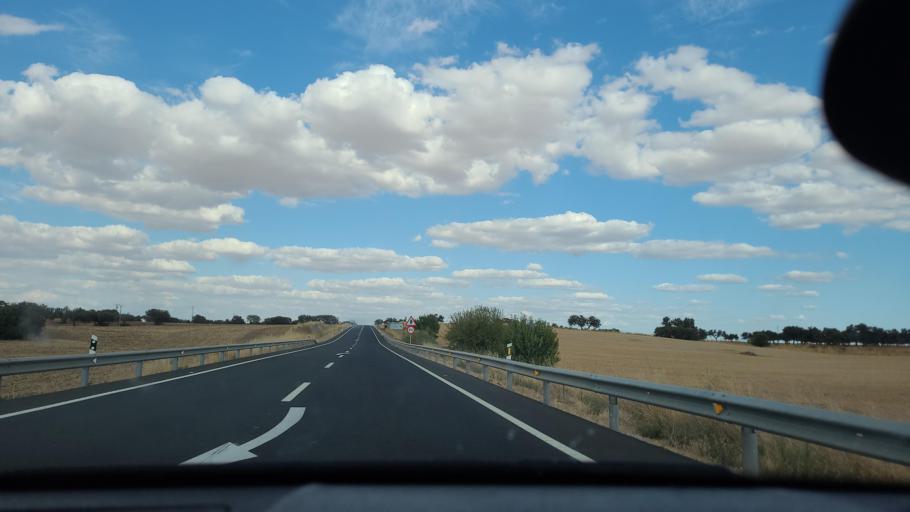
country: ES
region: Extremadura
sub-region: Provincia de Badajoz
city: Casas de Reina
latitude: 38.2493
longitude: -5.9467
